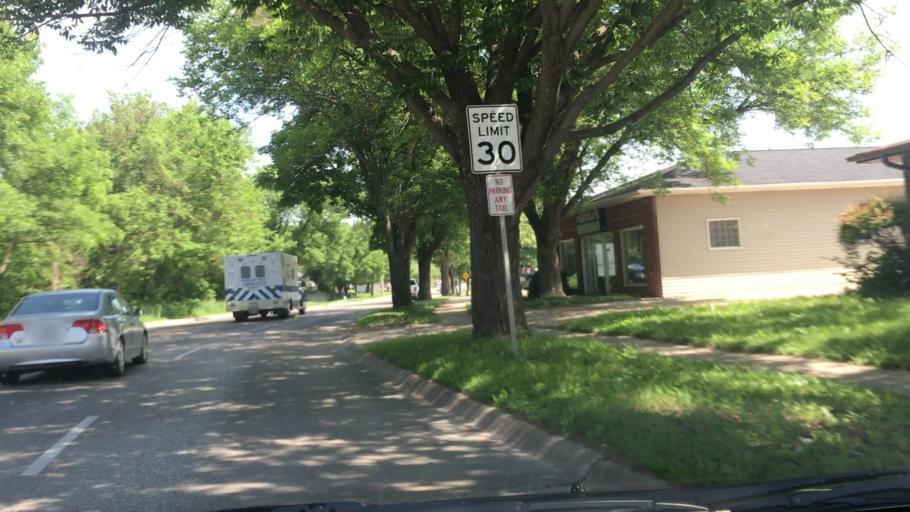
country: US
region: Iowa
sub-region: Johnson County
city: Iowa City
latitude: 41.6501
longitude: -91.5320
